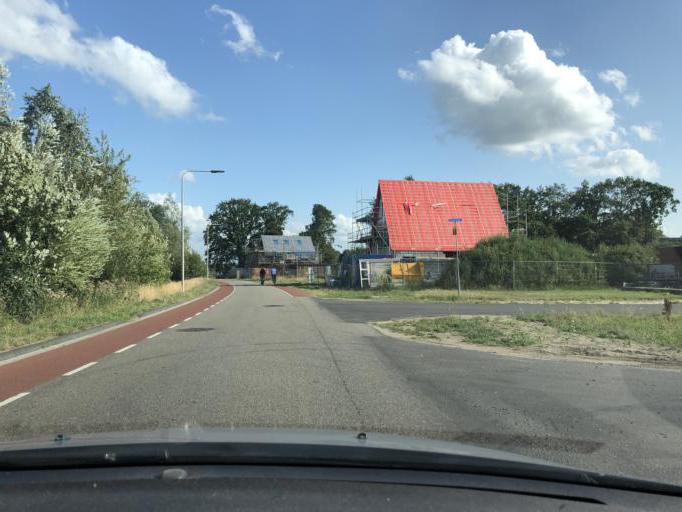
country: NL
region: Overijssel
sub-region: Gemeente Dalfsen
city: Dalfsen
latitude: 52.5829
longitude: 6.2756
